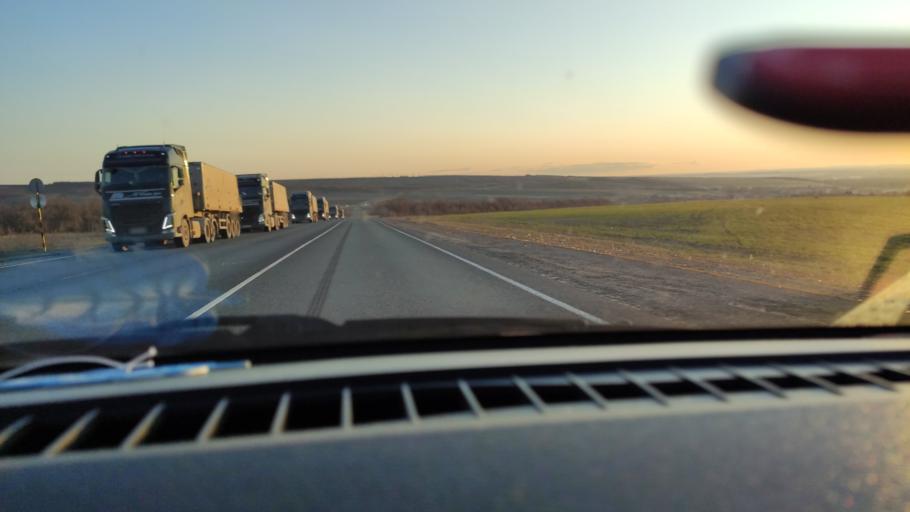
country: RU
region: Saratov
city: Sinodskoye
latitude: 51.9080
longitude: 46.5508
